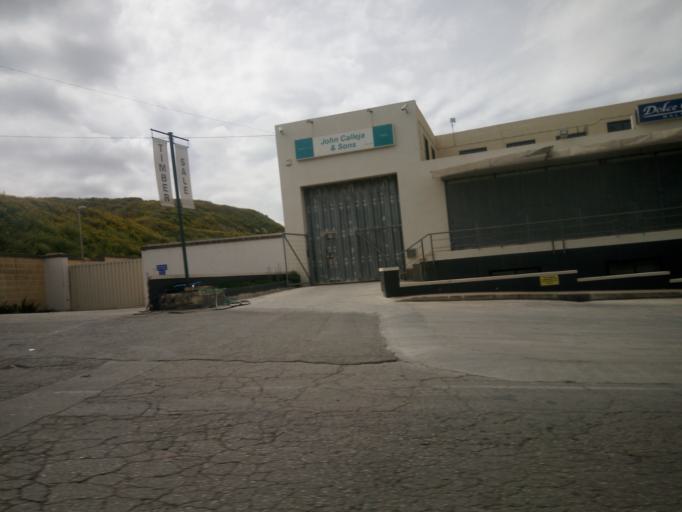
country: MT
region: Luqa
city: Luqa
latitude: 35.8684
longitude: 14.4897
